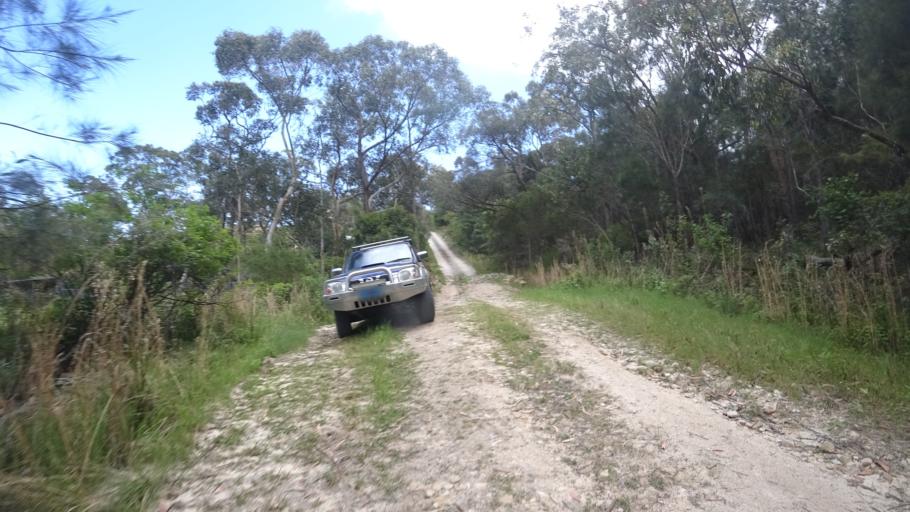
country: AU
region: New South Wales
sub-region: City of Sydney
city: North Turramurra
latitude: -33.6788
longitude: 151.1929
